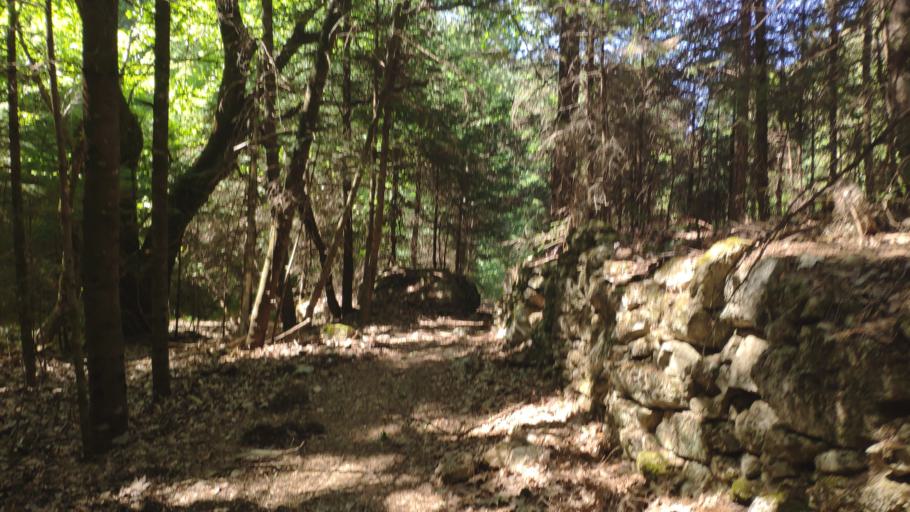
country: GR
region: Peloponnese
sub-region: Nomos Lakonias
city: Kariai
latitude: 37.1717
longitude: 22.5719
